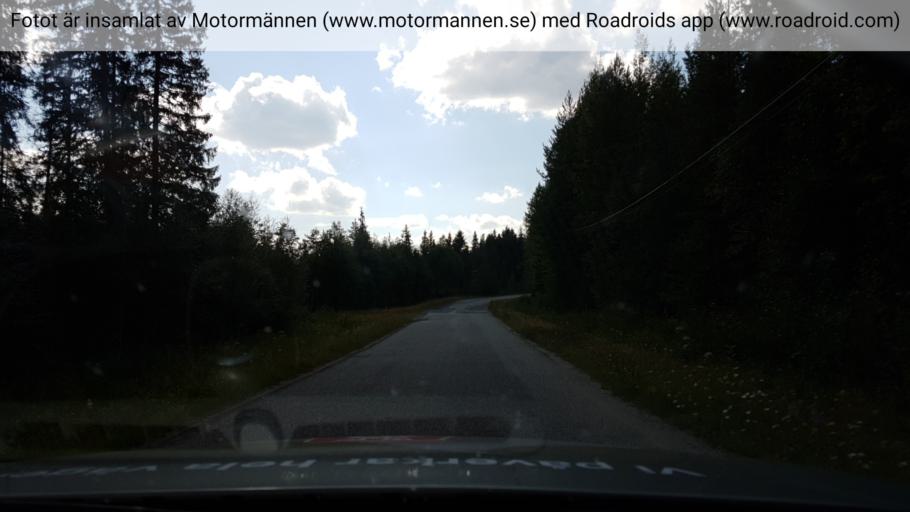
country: SE
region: Vaesterbotten
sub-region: Dorotea Kommun
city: Dorotea
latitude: 64.1280
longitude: 16.2313
